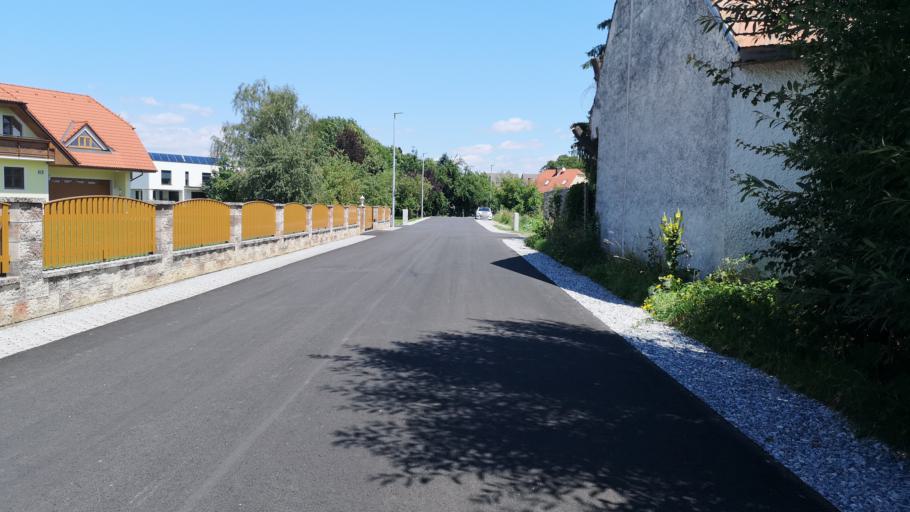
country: AT
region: Styria
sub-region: Politischer Bezirk Graz-Umgebung
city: Feldkirchen bei Graz
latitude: 47.0267
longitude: 15.4615
